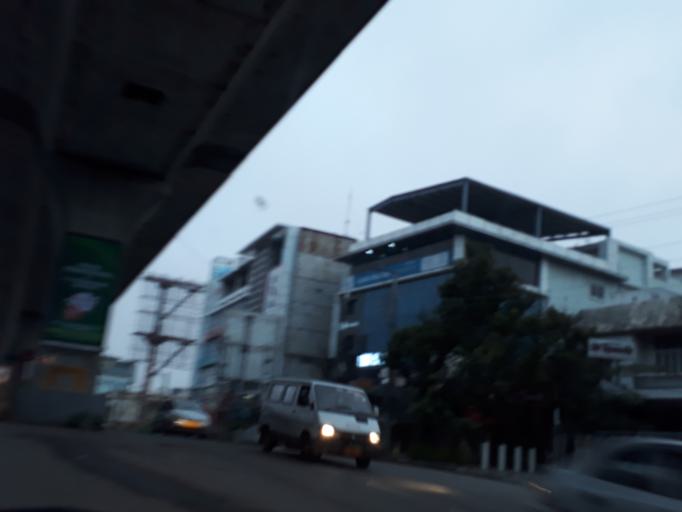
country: IN
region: Telangana
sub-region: Rangareddi
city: Kukatpalli
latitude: 17.4334
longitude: 78.4057
